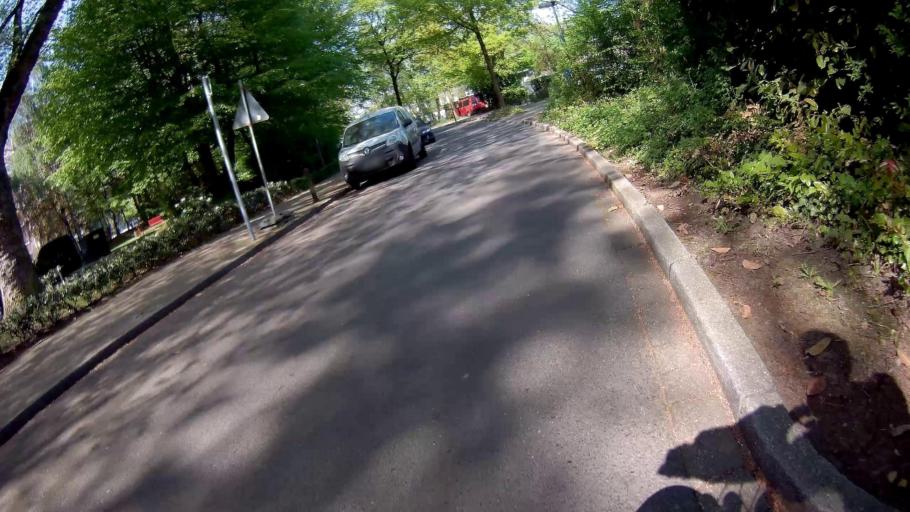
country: DE
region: North Rhine-Westphalia
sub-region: Regierungsbezirk Munster
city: Gladbeck
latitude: 51.5853
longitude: 7.0614
